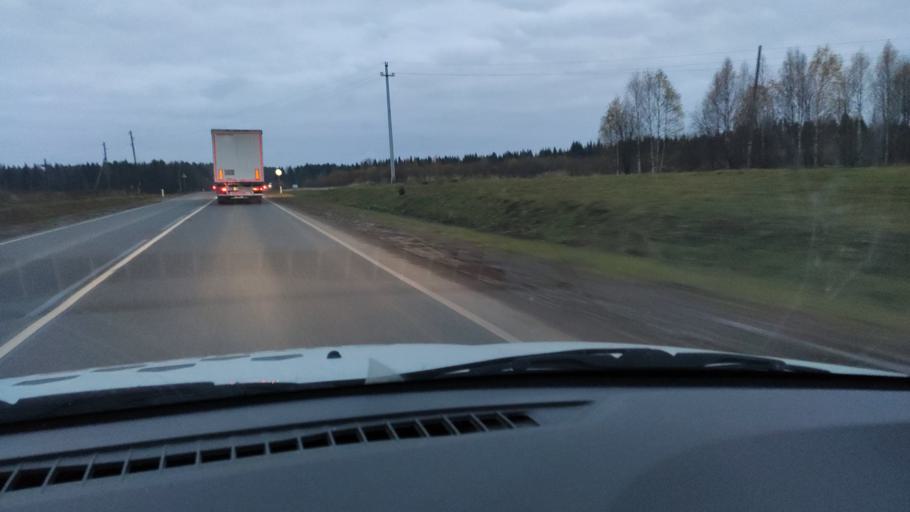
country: RU
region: Kirov
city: Kostino
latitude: 58.8475
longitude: 53.2978
